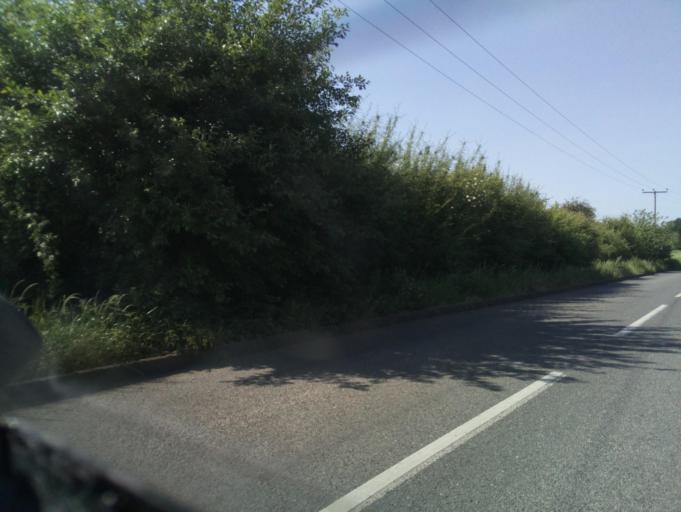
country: GB
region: England
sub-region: Hampshire
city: Abbotts Ann
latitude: 51.2292
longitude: -1.5650
